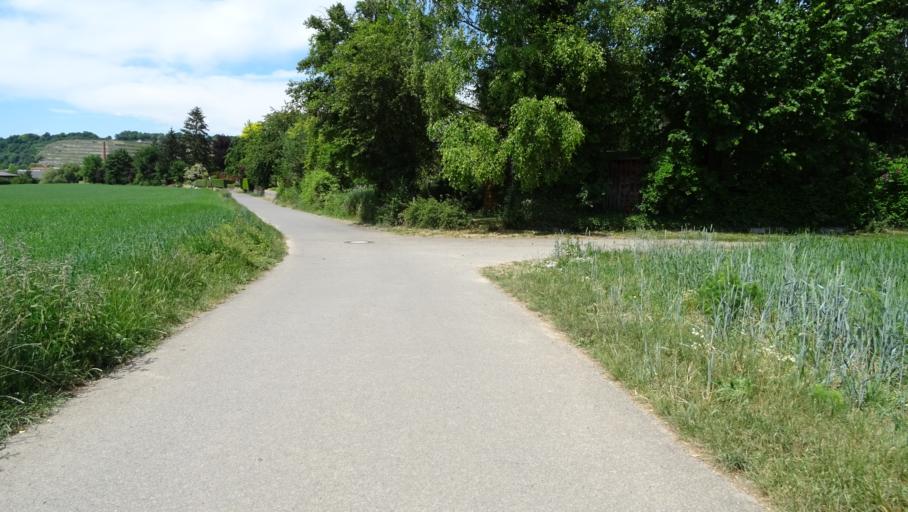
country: DE
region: Baden-Wuerttemberg
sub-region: Regierungsbezirk Stuttgart
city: Gundelsheim
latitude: 49.2764
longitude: 9.1639
